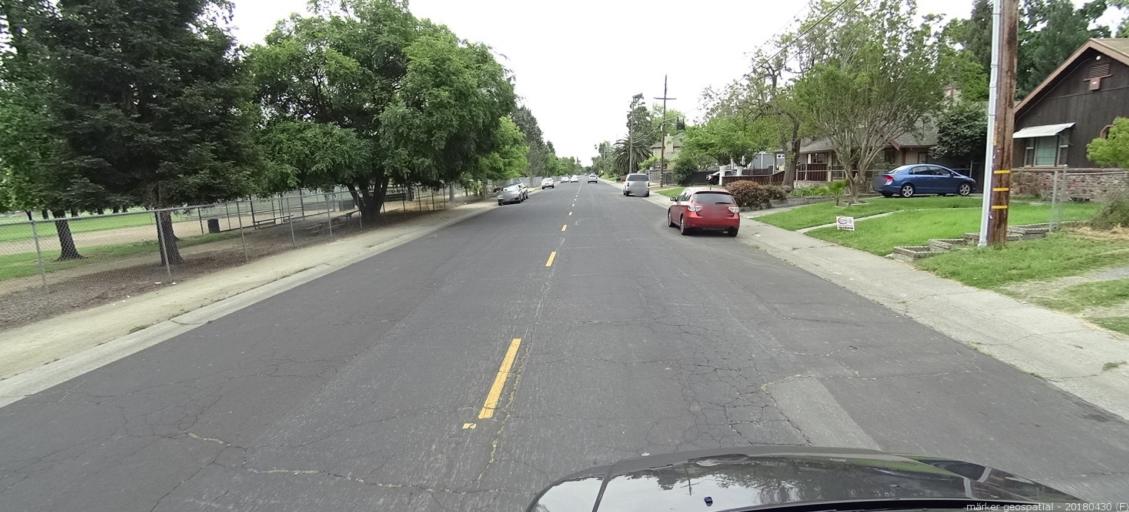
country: US
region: California
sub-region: Yolo County
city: West Sacramento
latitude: 38.6008
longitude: -121.5361
